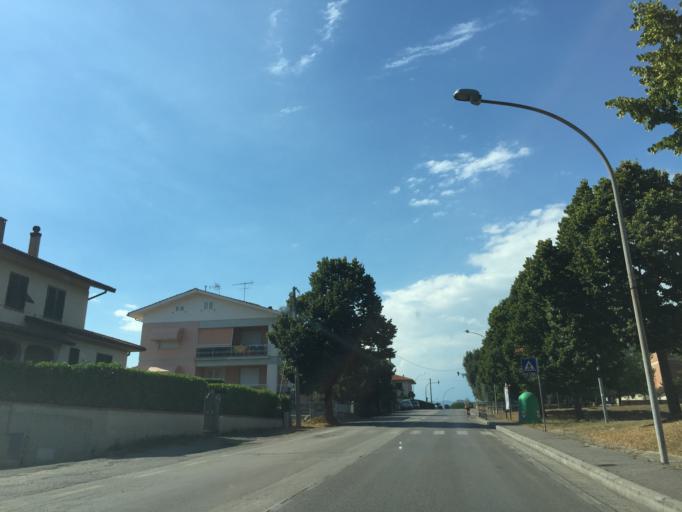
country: IT
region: Tuscany
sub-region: Provincia di Pistoia
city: San Rocco
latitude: 43.8215
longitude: 10.8725
